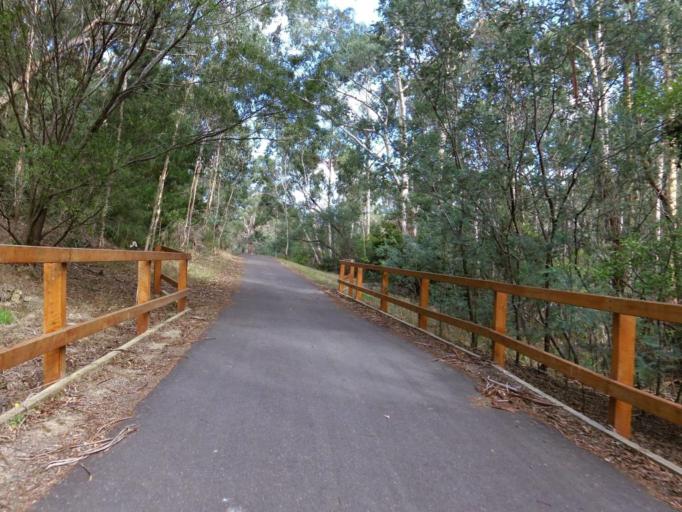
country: AU
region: Victoria
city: Mitcham
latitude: -37.8015
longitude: 145.2030
